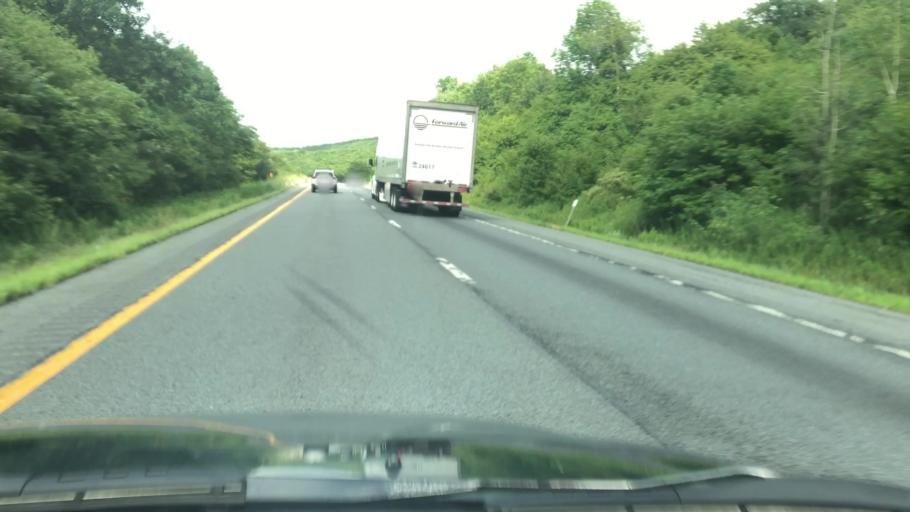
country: US
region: New York
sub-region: Orange County
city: Port Jervis
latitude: 41.3566
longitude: -74.6680
